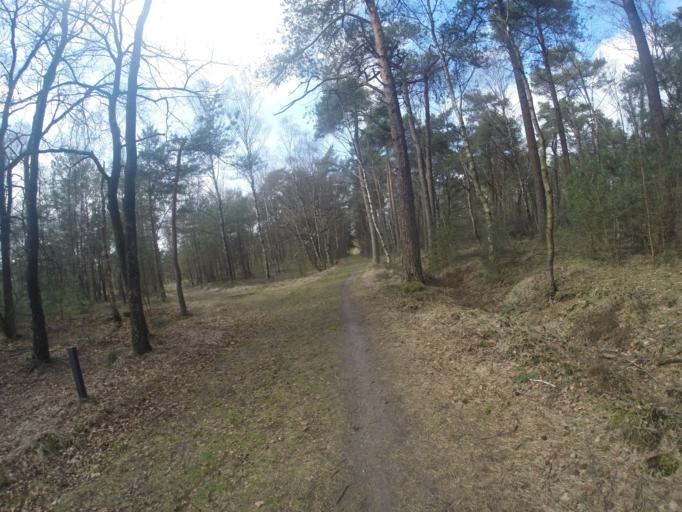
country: NL
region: Gelderland
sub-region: Gemeente Lochem
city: Almen
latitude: 52.1460
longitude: 6.3254
